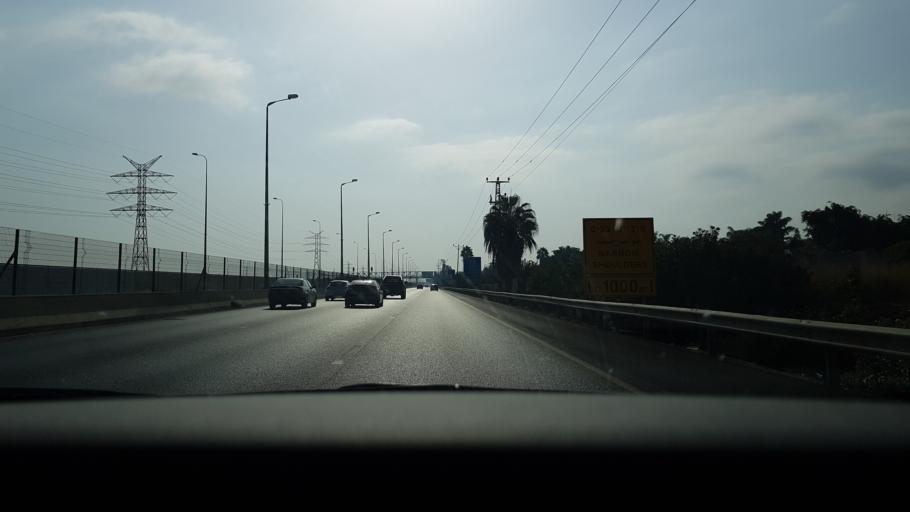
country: IL
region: Tel Aviv
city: Azor
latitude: 32.0320
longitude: 34.8019
